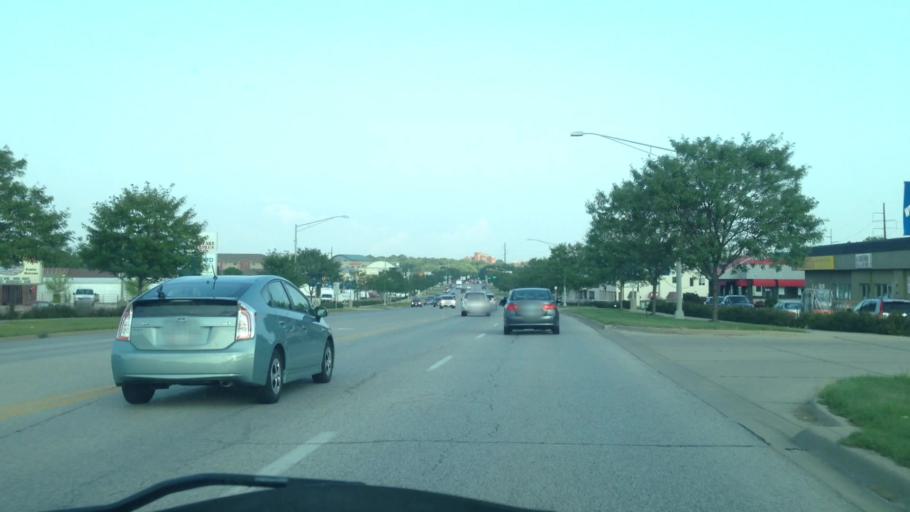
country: US
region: Iowa
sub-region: Johnson County
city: Coralville
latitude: 41.6726
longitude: -91.5779
